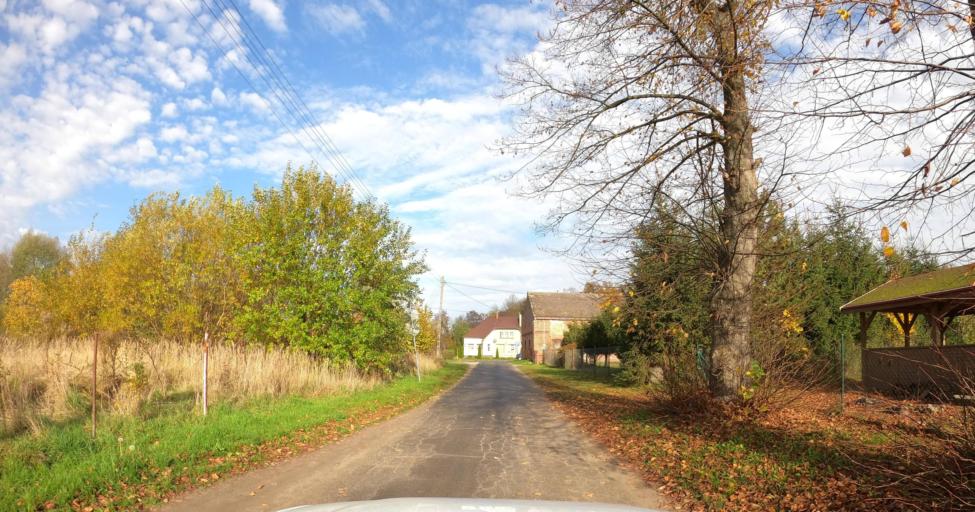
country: PL
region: West Pomeranian Voivodeship
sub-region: Powiat kamienski
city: Golczewo
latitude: 53.8610
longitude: 14.9113
